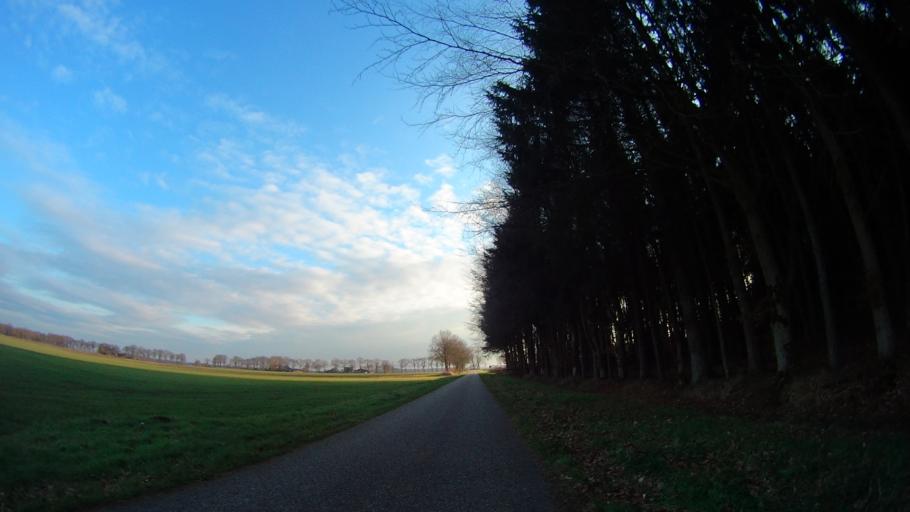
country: NL
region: Drenthe
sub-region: Gemeente Coevorden
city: Sleen
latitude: 52.7957
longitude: 6.7679
